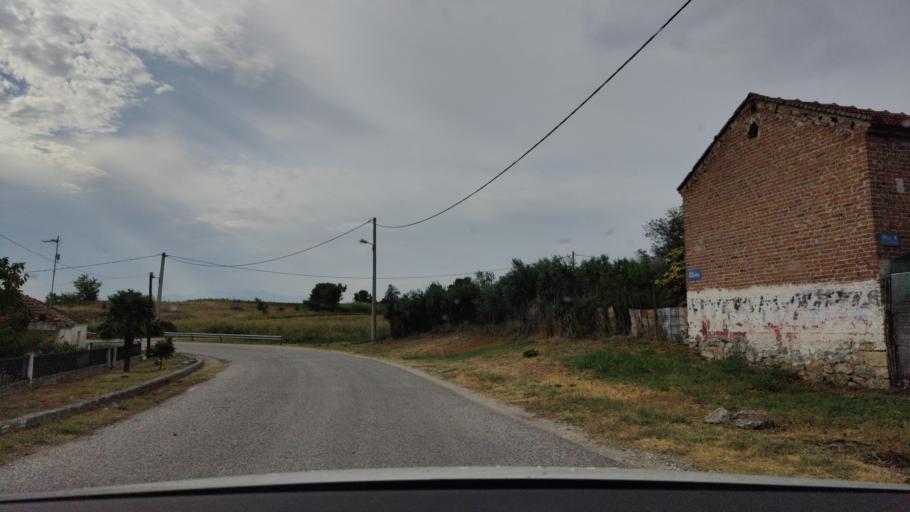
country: GR
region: Central Macedonia
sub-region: Nomos Serron
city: Kala Dendra
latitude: 41.1212
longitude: 23.4598
